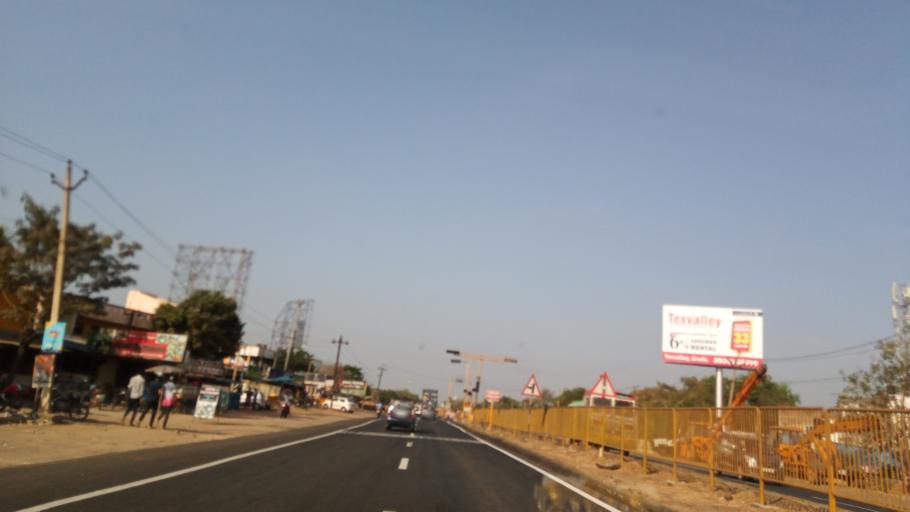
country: IN
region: Tamil Nadu
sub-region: Kancheepuram
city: Nandambakkam
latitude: 13.0237
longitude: 80.0225
